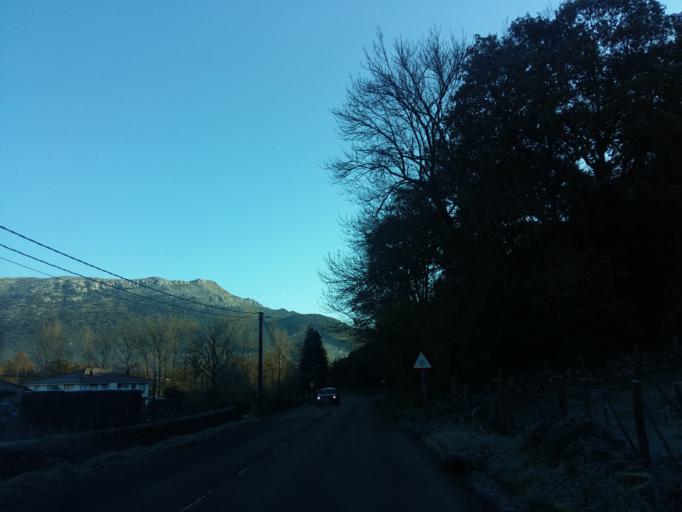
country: ES
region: Cantabria
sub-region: Provincia de Cantabria
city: Arredondo
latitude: 43.2820
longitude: -3.5498
